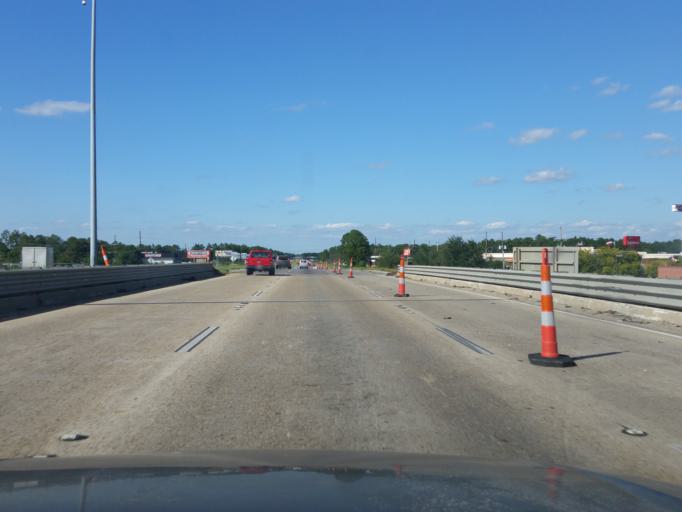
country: US
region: Louisiana
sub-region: Saint Tammany Parish
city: Slidell
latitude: 30.2846
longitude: -89.7495
